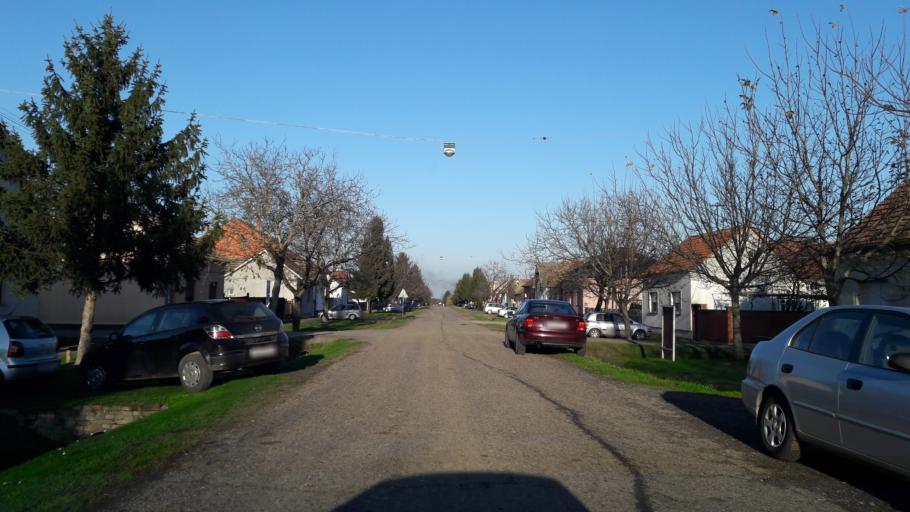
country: HR
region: Osjecko-Baranjska
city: Viskovci
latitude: 45.3389
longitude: 18.4512
